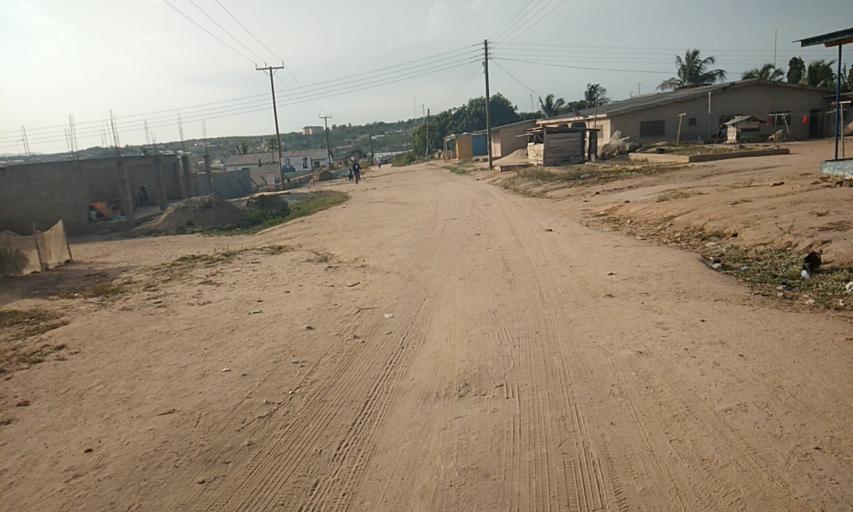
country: GH
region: Central
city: Winneba
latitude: 5.3571
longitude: -0.6141
